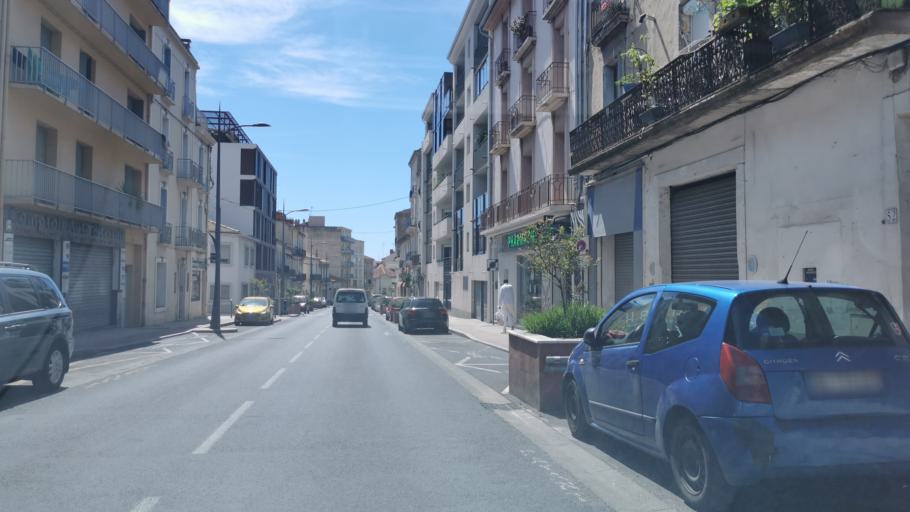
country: FR
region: Languedoc-Roussillon
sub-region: Departement de l'Herault
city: Beziers
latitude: 43.3399
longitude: 3.2236
